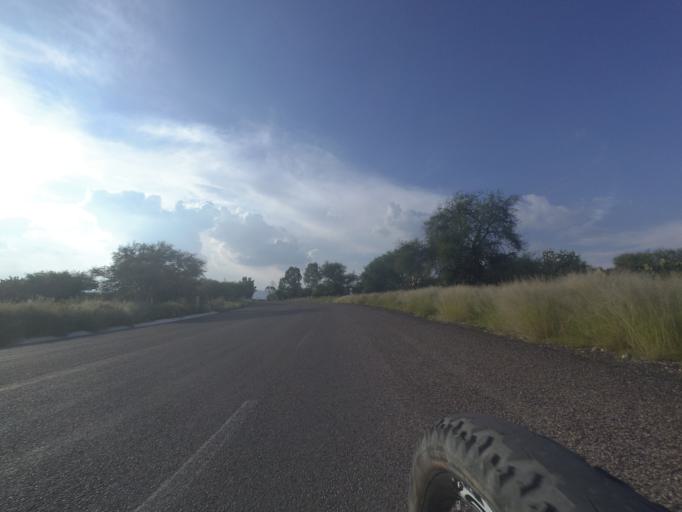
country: MX
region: Aguascalientes
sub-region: Aguascalientes
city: Penuelas (El Cienegal)
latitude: 21.7638
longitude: -102.3520
